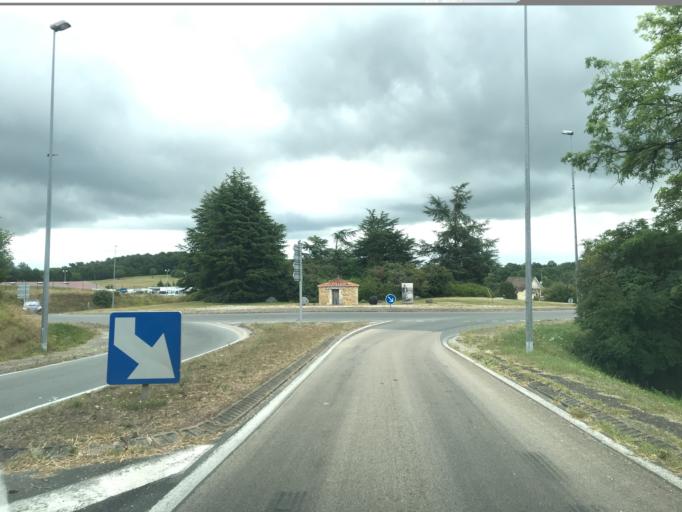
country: FR
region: Aquitaine
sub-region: Departement de la Dordogne
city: Brantome
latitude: 45.3784
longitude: 0.6414
